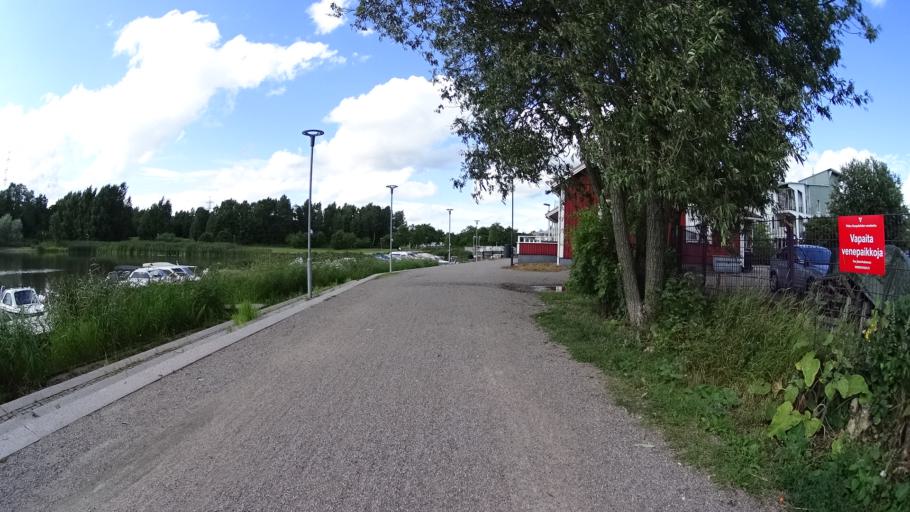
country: FI
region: Uusimaa
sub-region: Helsinki
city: Helsinki
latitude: 60.2013
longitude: 24.8921
